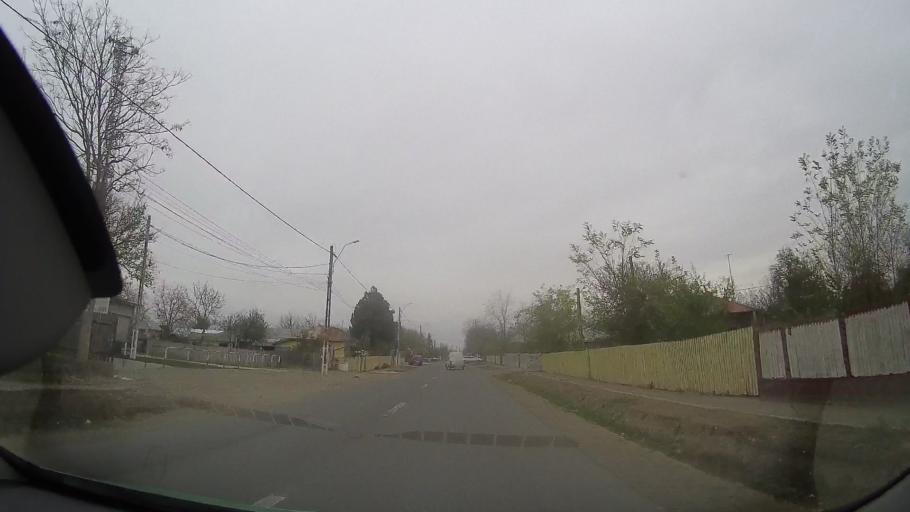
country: RO
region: Braila
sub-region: Comuna Budesti
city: Tataru
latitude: 44.8478
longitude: 27.4290
